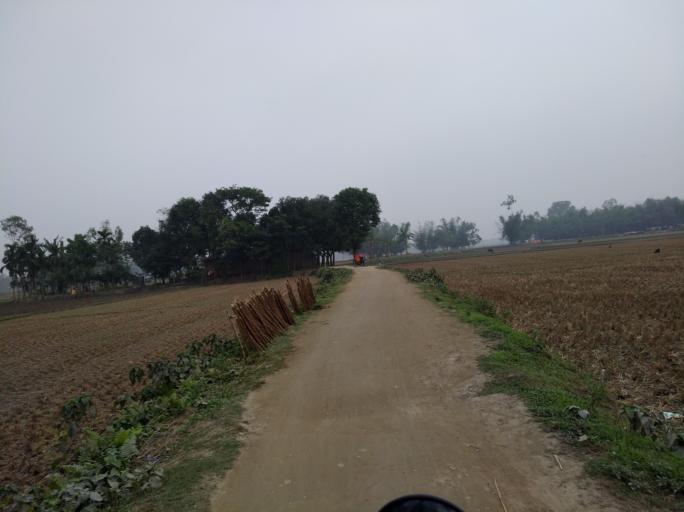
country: BD
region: Rajshahi
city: Saidpur
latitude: 25.9830
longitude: 88.9120
